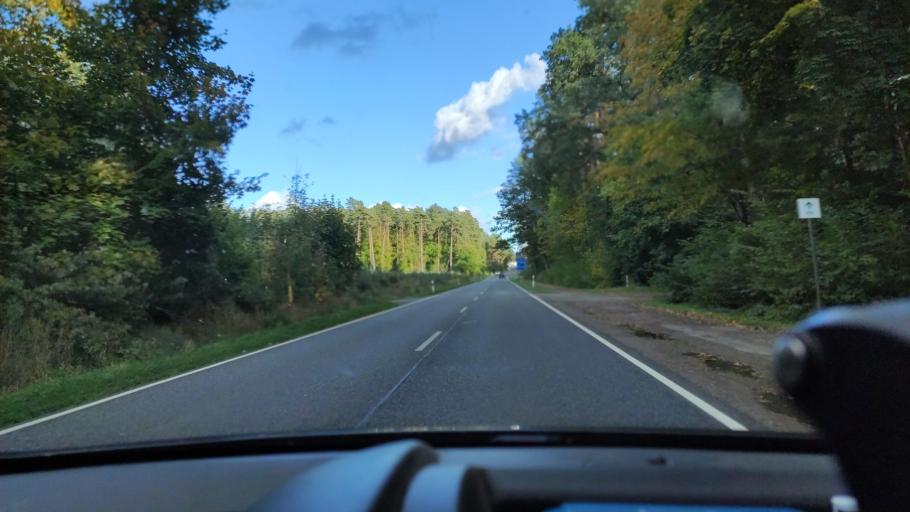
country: DE
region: Mecklenburg-Vorpommern
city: Lalendorf
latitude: 53.7732
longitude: 12.3114
